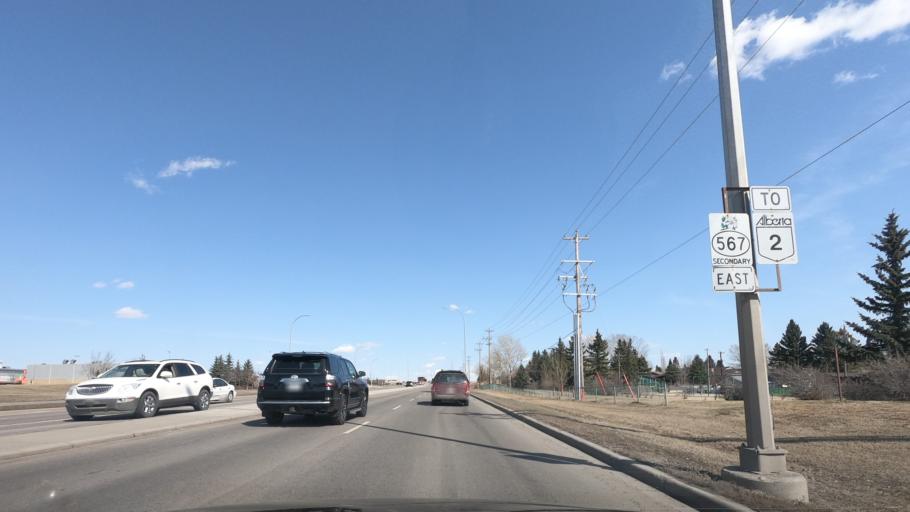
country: CA
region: Alberta
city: Airdrie
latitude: 51.3000
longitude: -114.0126
